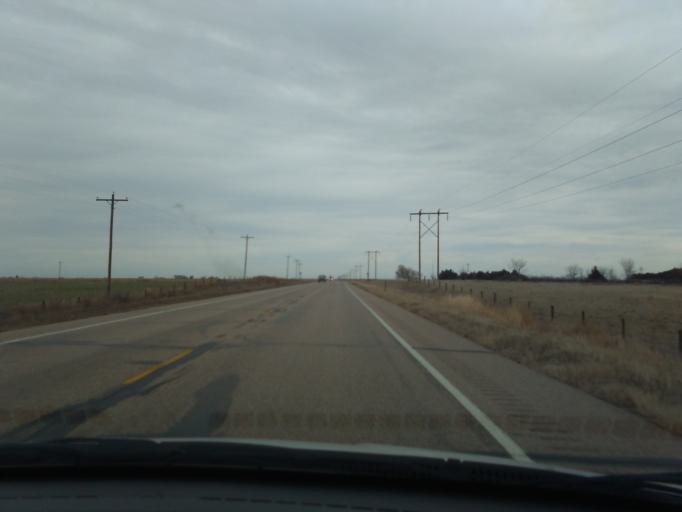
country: US
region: Colorado
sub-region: Yuma County
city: Yuma
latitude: 40.1482
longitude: -102.8619
